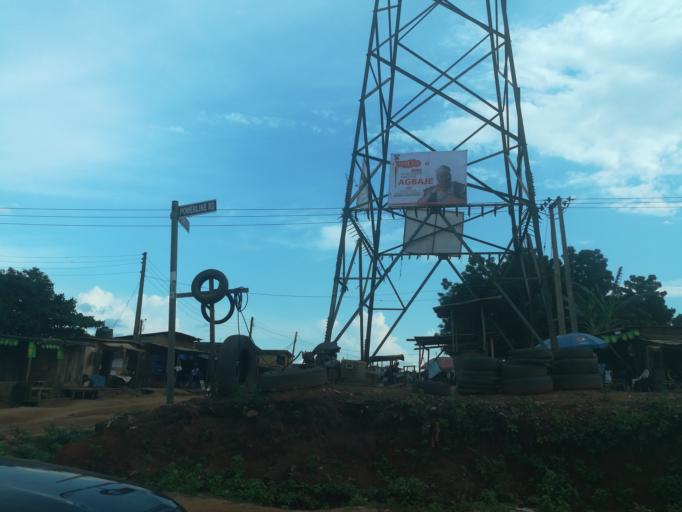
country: NG
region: Lagos
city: Ikorodu
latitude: 6.6259
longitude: 3.5010
